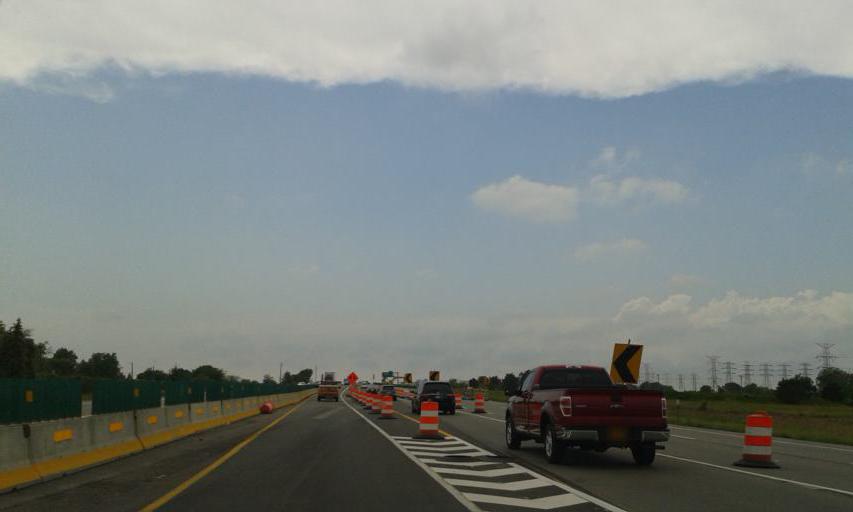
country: US
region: New York
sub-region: Erie County
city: Tonawanda
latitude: 42.9957
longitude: -78.8691
